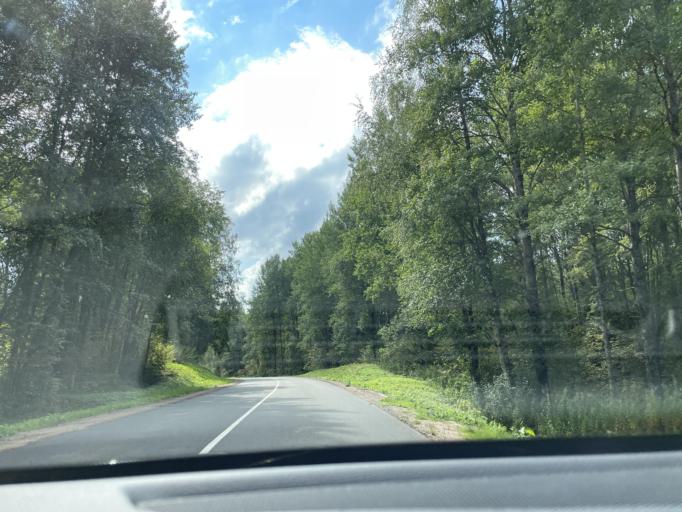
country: RU
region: Novgorod
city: Valday
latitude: 58.0119
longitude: 33.1775
